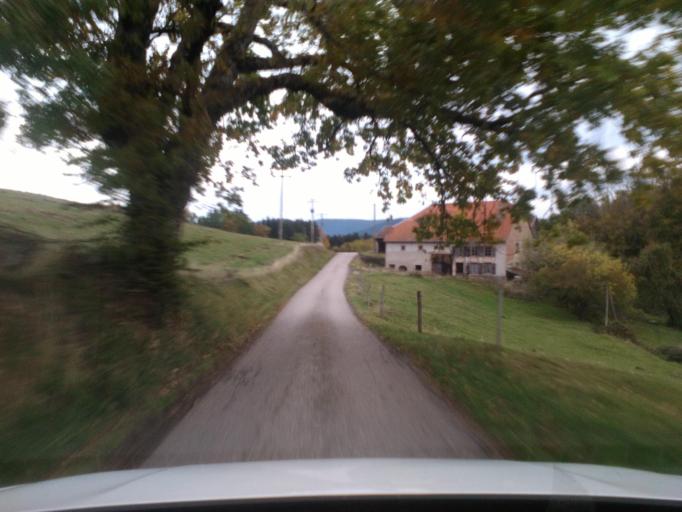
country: FR
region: Lorraine
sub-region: Departement des Vosges
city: Senones
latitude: 48.3719
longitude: 7.0285
